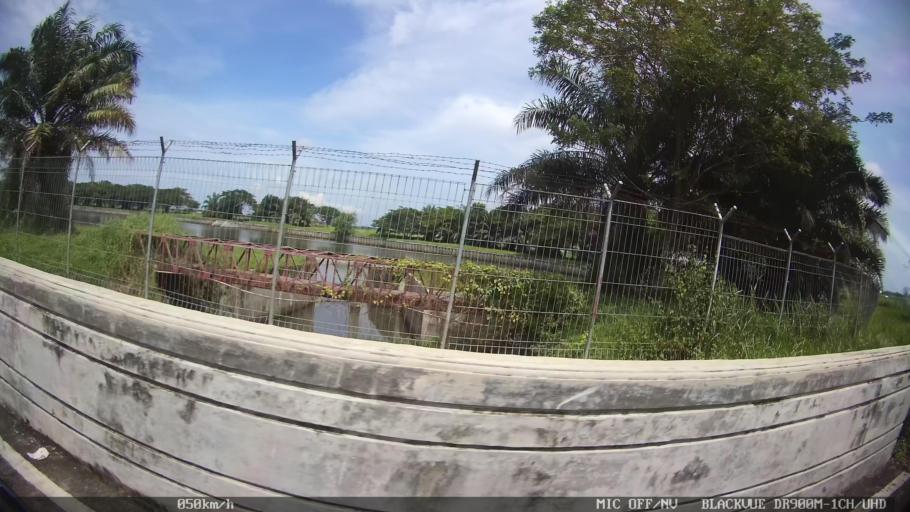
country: ID
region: North Sumatra
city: Percut
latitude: 3.6330
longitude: 98.8734
